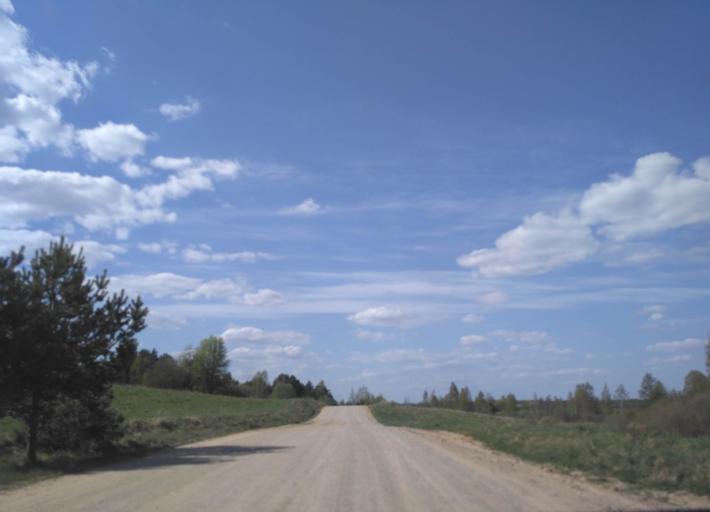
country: BY
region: Minsk
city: Narach
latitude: 54.9755
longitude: 26.6239
